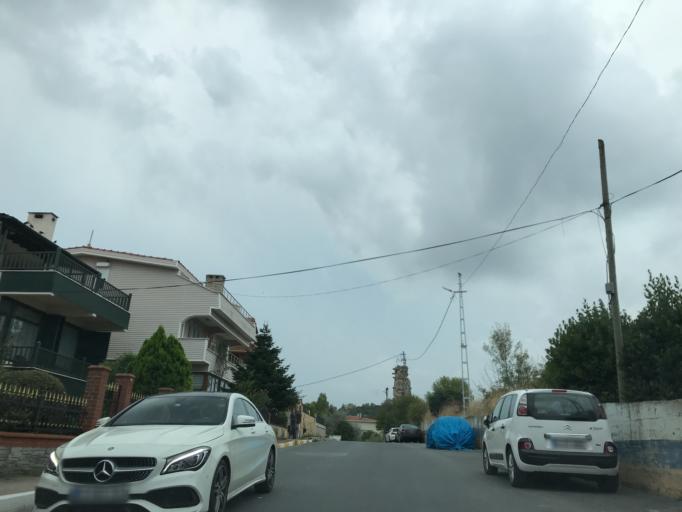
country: TR
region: Istanbul
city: Arikoey
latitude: 41.2452
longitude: 29.0335
